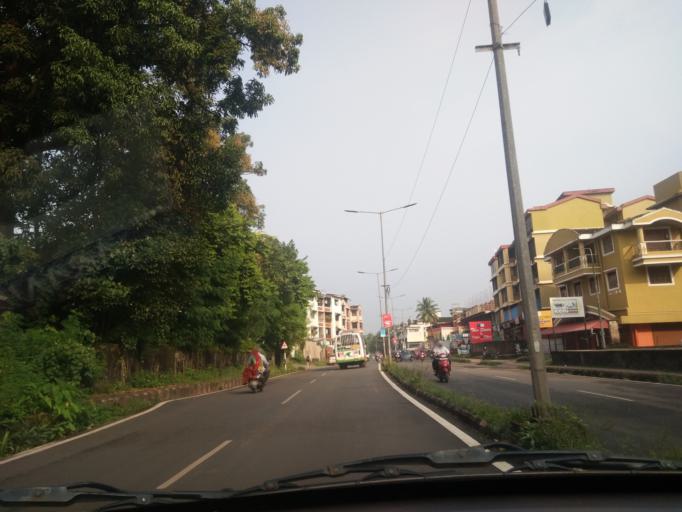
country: IN
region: Goa
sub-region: South Goa
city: Madgaon
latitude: 15.2608
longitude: 73.9638
